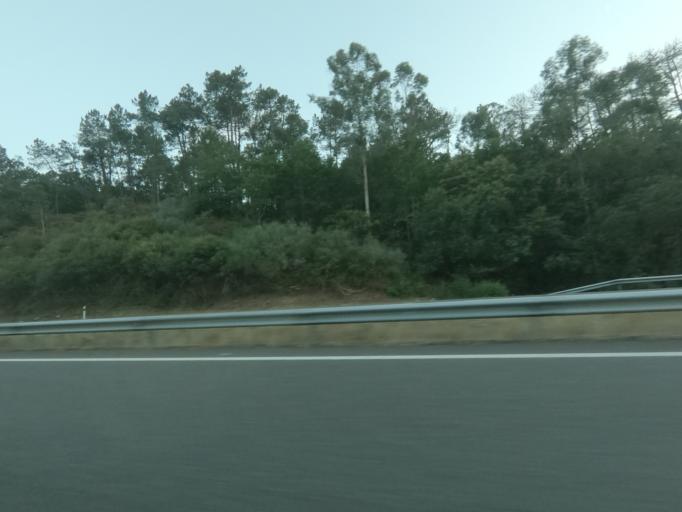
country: ES
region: Galicia
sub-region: Provincia de Pontevedra
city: Ponteareas
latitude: 42.1687
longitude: -8.5409
